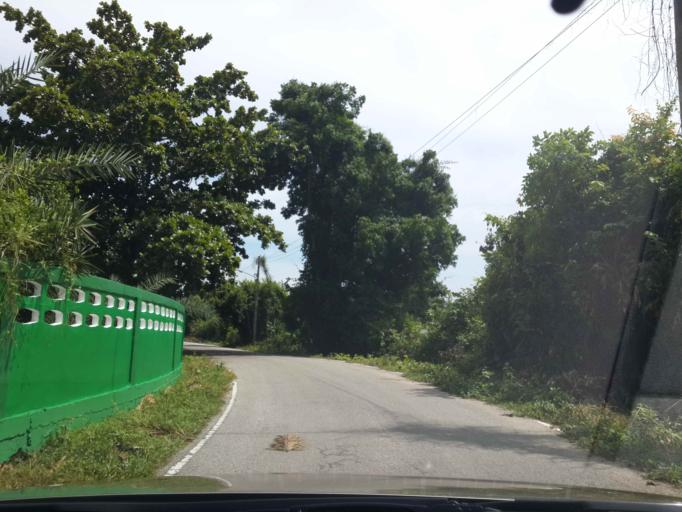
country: TH
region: Narathiwat
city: Rueso
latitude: 6.4002
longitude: 101.5160
